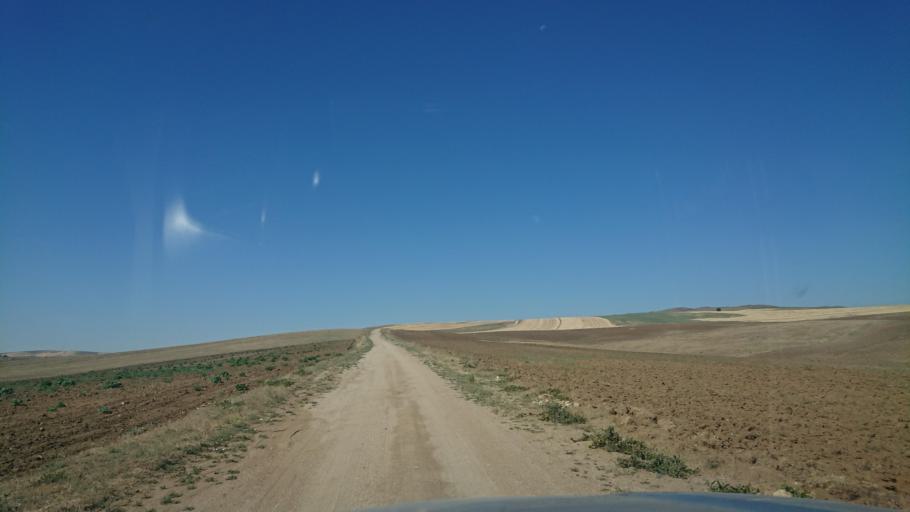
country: TR
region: Aksaray
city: Sariyahsi
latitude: 38.9300
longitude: 33.8565
